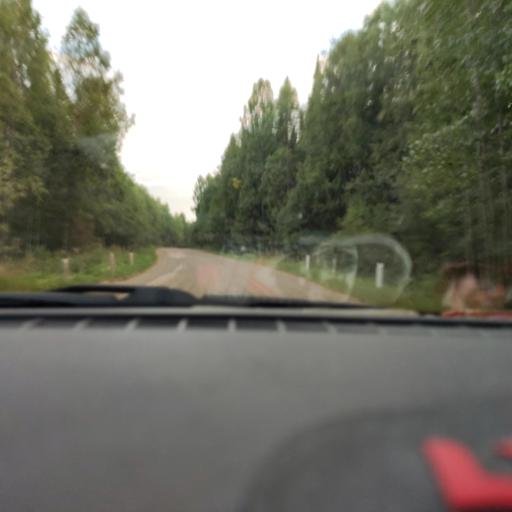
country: RU
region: Perm
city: Pavlovskiy
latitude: 57.9843
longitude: 54.8605
